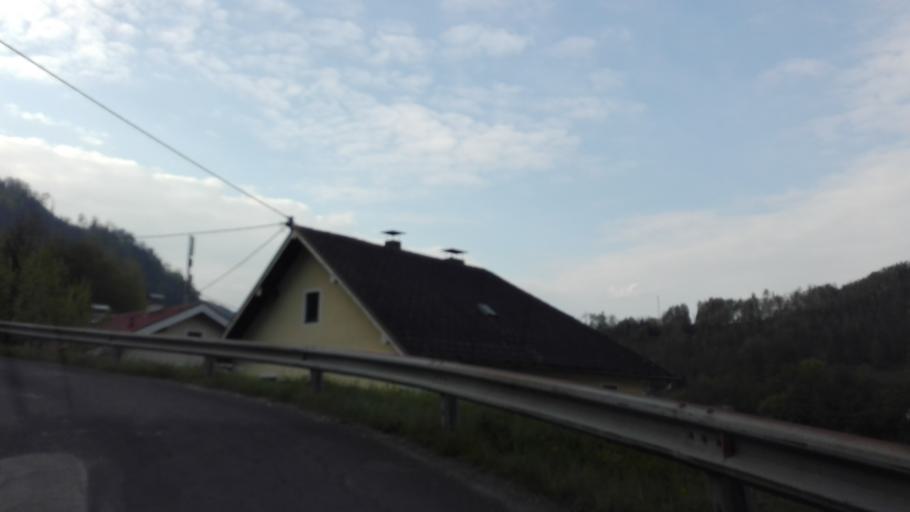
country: AT
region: Upper Austria
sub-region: Politischer Bezirk Steyr-Land
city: Ternberg
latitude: 47.9297
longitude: 14.3549
